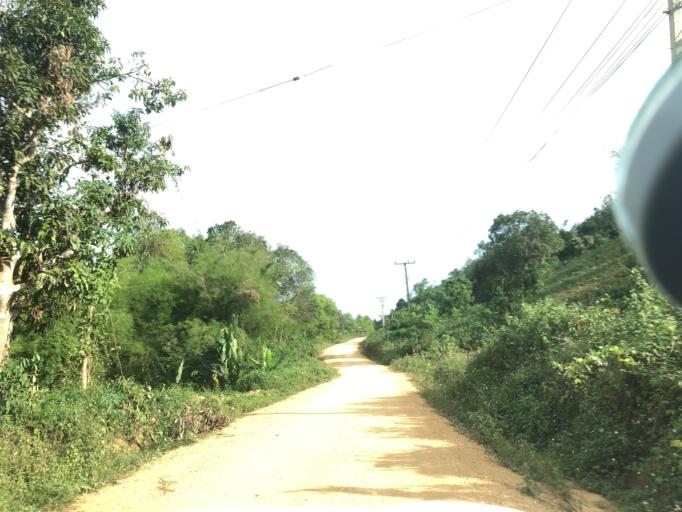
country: TH
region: Loei
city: Chiang Khan
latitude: 18.0242
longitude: 101.4184
